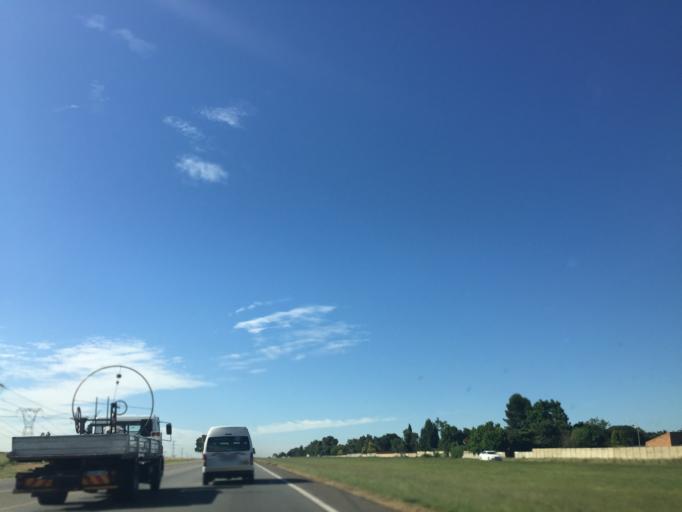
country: ZA
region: Gauteng
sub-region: Ekurhuleni Metropolitan Municipality
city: Germiston
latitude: -26.3107
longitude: 28.1125
